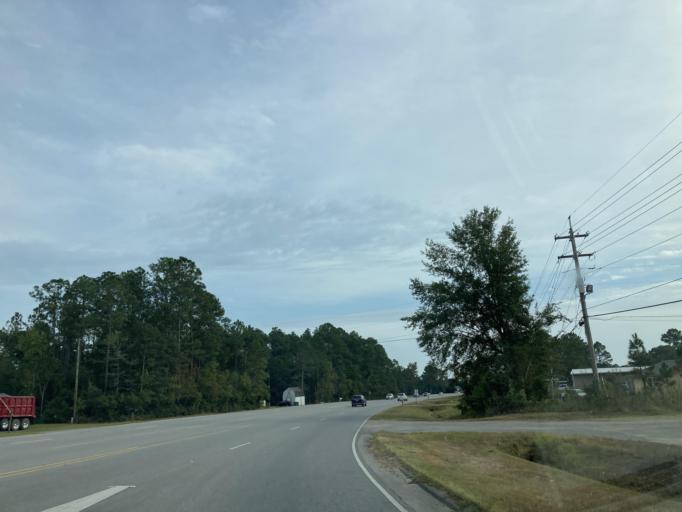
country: US
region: Mississippi
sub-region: Jackson County
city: Saint Martin
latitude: 30.4792
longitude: -88.8508
